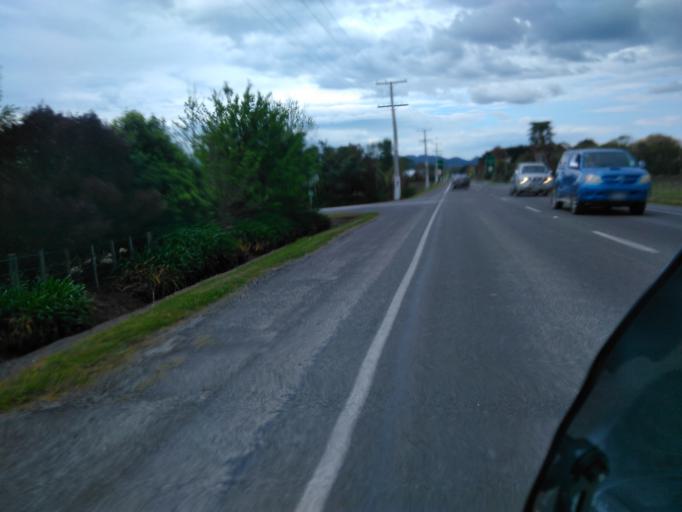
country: NZ
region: Gisborne
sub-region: Gisborne District
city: Gisborne
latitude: -38.6531
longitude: 177.9569
